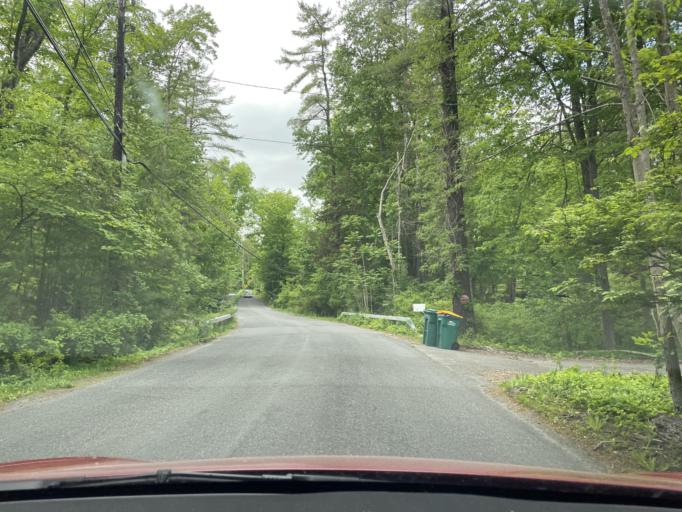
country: US
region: New York
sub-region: Ulster County
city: West Hurley
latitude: 42.0196
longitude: -74.0996
